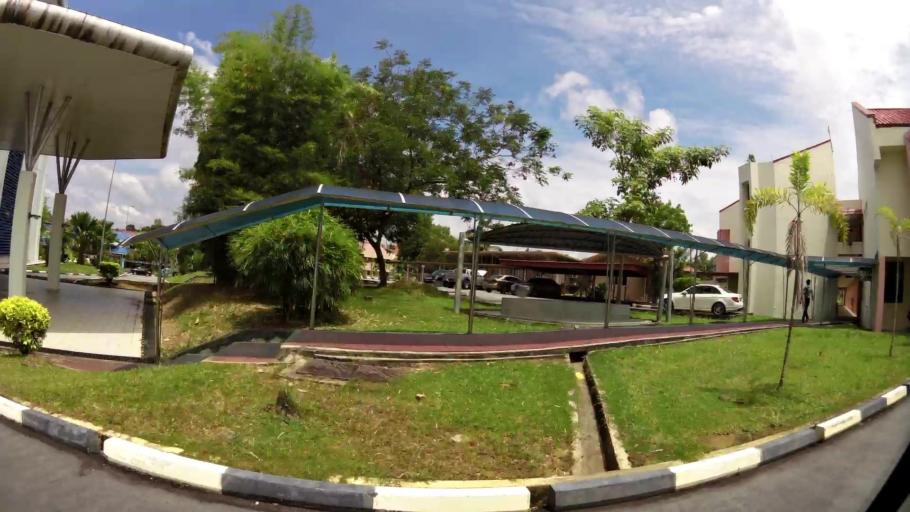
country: BN
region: Brunei and Muara
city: Bandar Seri Begawan
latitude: 4.9024
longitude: 114.9127
